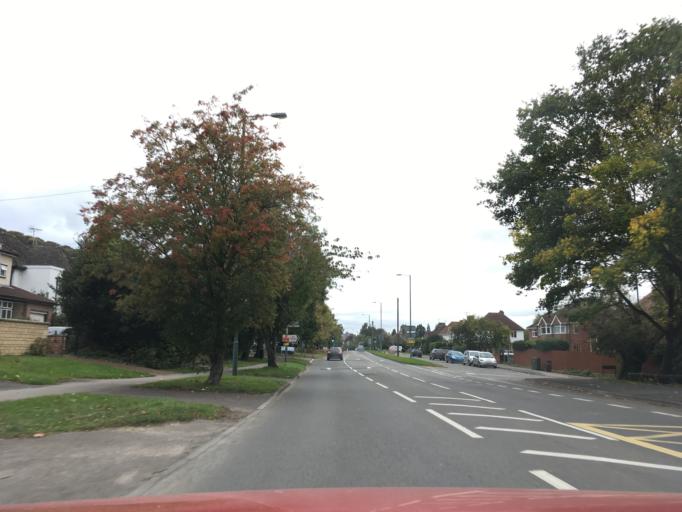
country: GB
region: England
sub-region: Gloucestershire
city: Dursley
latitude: 51.6876
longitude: -2.3599
